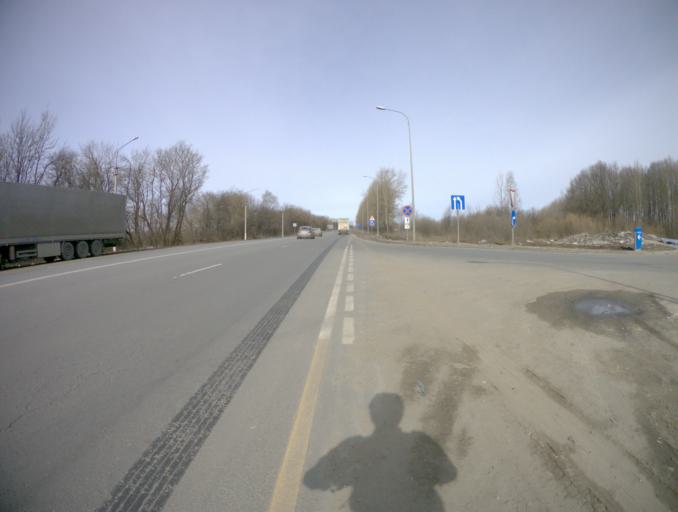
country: RU
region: Vladimir
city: Kommunar
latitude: 56.1786
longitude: 40.4538
